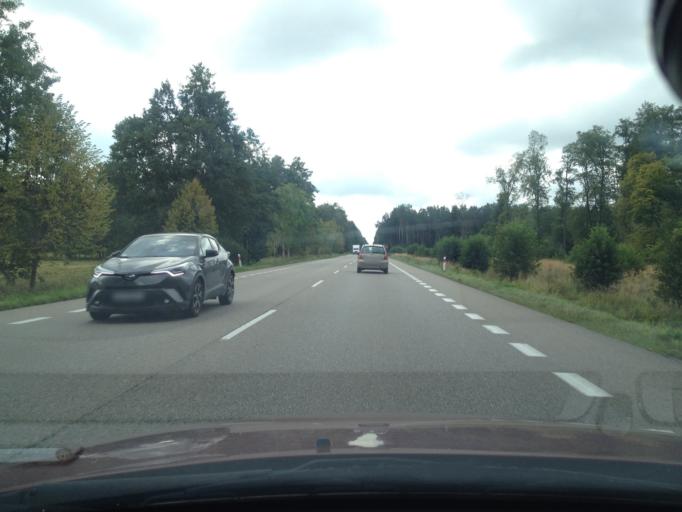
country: PL
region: West Pomeranian Voivodeship
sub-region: Powiat goleniowski
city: Przybiernow
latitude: 53.6628
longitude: 14.8150
